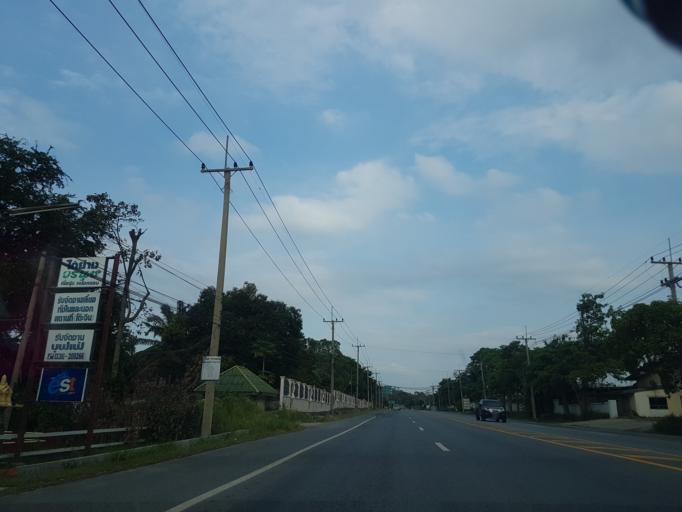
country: TH
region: Sara Buri
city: Phra Phutthabat
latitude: 14.7177
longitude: 100.7970
